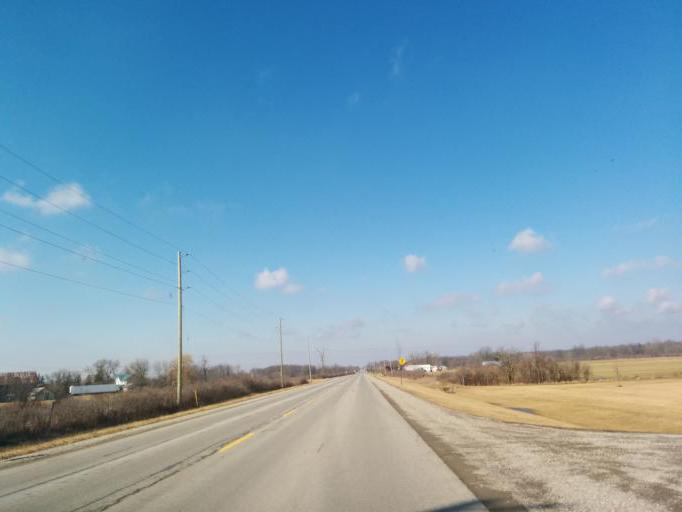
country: CA
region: Ontario
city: Brantford
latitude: 42.9944
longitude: -80.1397
